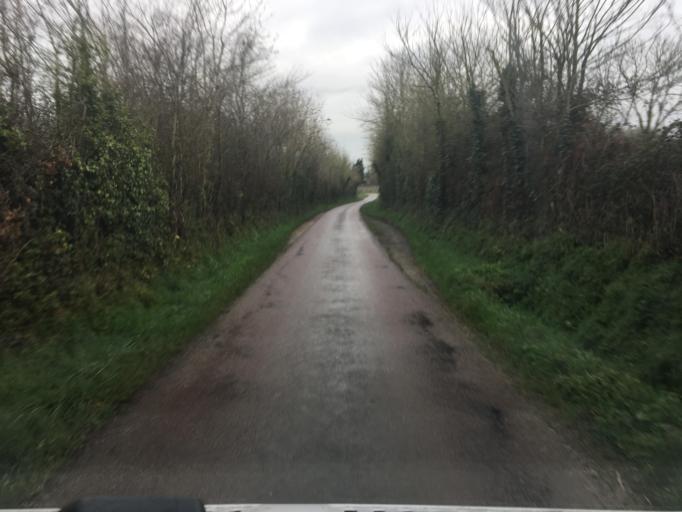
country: FR
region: Lower Normandy
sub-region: Departement de la Manche
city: Sainte-Mere-Eglise
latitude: 49.4245
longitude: -1.2671
